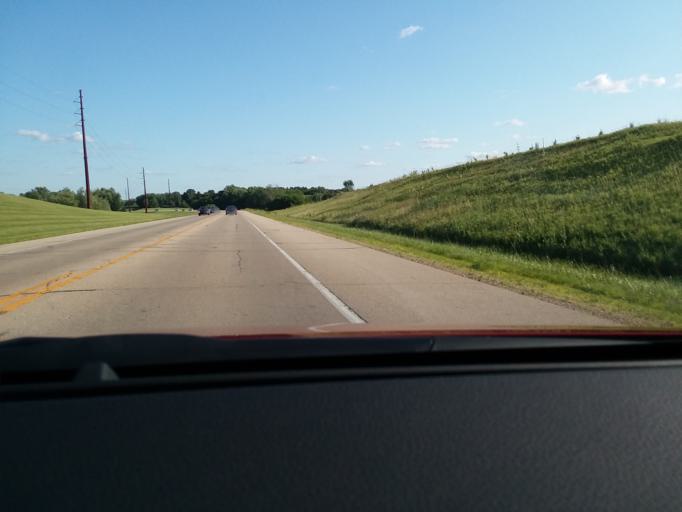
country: US
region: Wisconsin
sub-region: Dane County
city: Waunakee
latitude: 43.1764
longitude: -89.4117
